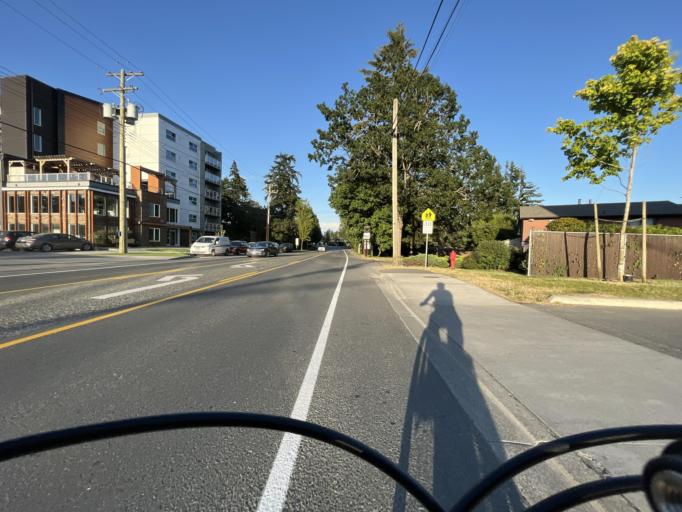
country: CA
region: British Columbia
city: Langford
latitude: 48.4495
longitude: -123.5165
